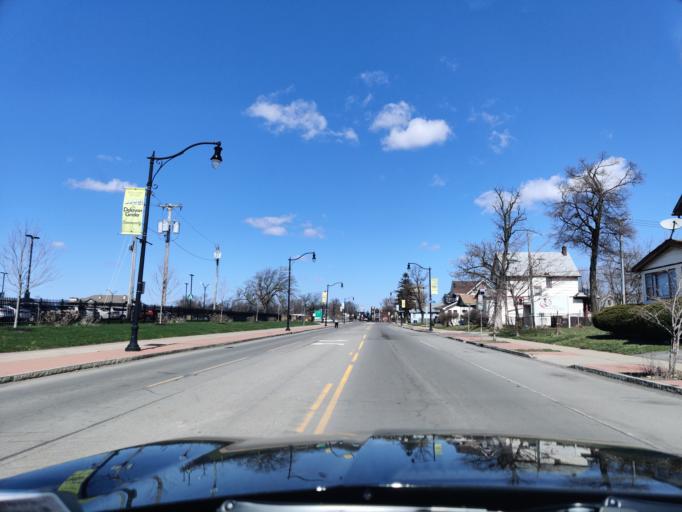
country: US
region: New York
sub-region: Erie County
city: Eggertsville
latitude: 42.9275
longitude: -78.8292
